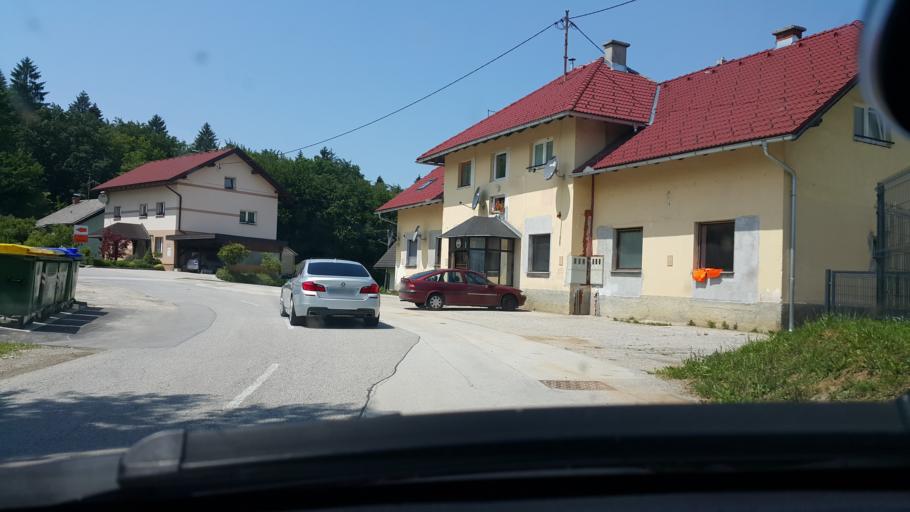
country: SI
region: Novo Mesto
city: Novo Mesto
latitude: 45.7639
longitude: 15.1517
